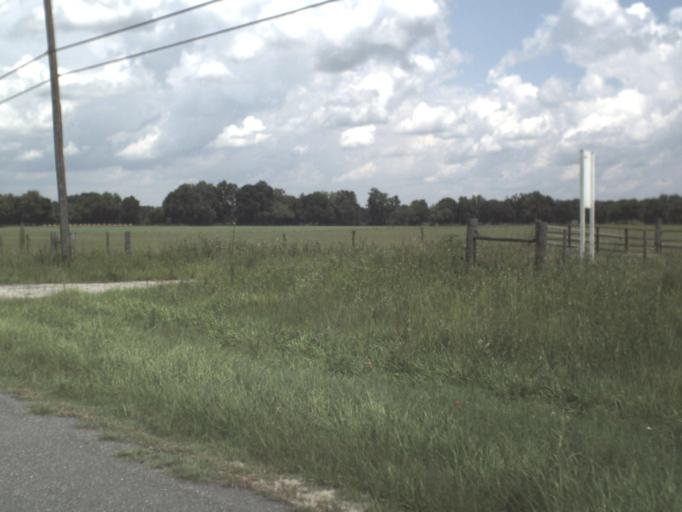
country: US
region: Florida
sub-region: Alachua County
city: Newberry
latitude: 29.6419
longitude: -82.6612
